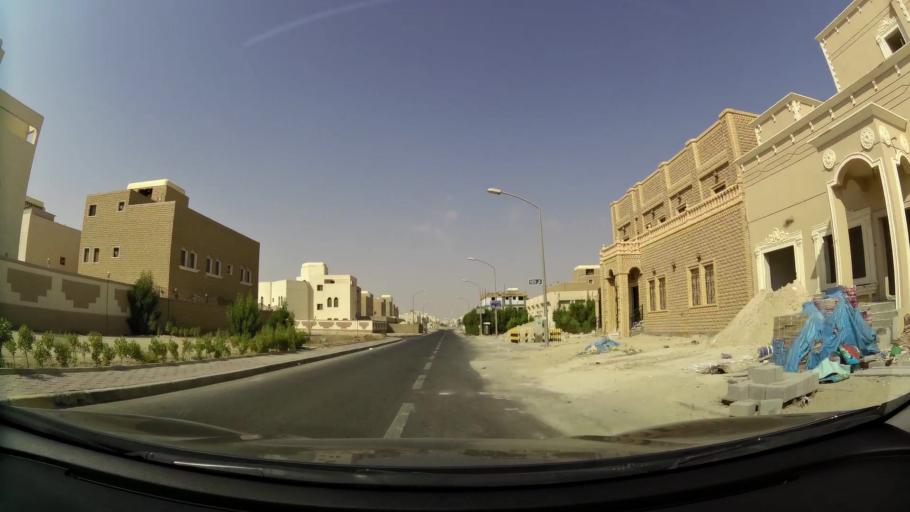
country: KW
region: Al Ahmadi
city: Al Wafrah
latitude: 28.8018
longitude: 48.0555
